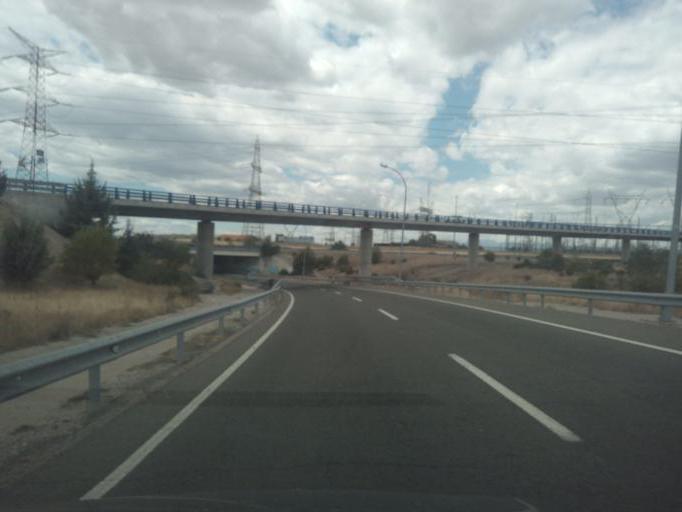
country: ES
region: Madrid
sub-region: Provincia de Madrid
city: San Sebastian de los Reyes
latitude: 40.5618
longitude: -3.5926
